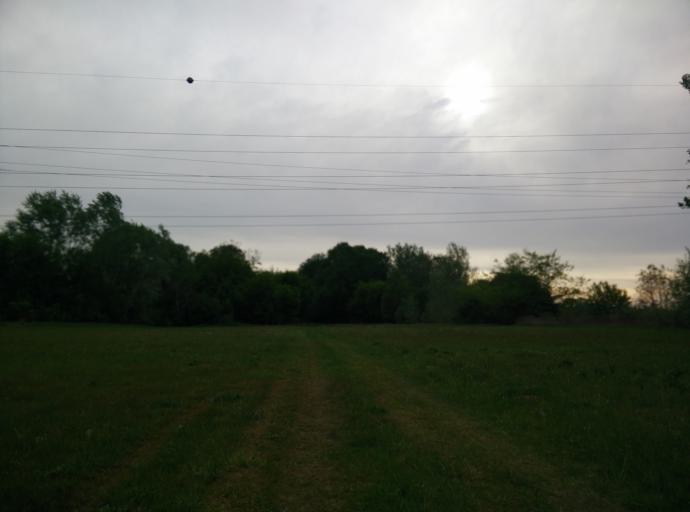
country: HU
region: Pest
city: Fot
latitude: 47.6070
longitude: 19.1749
